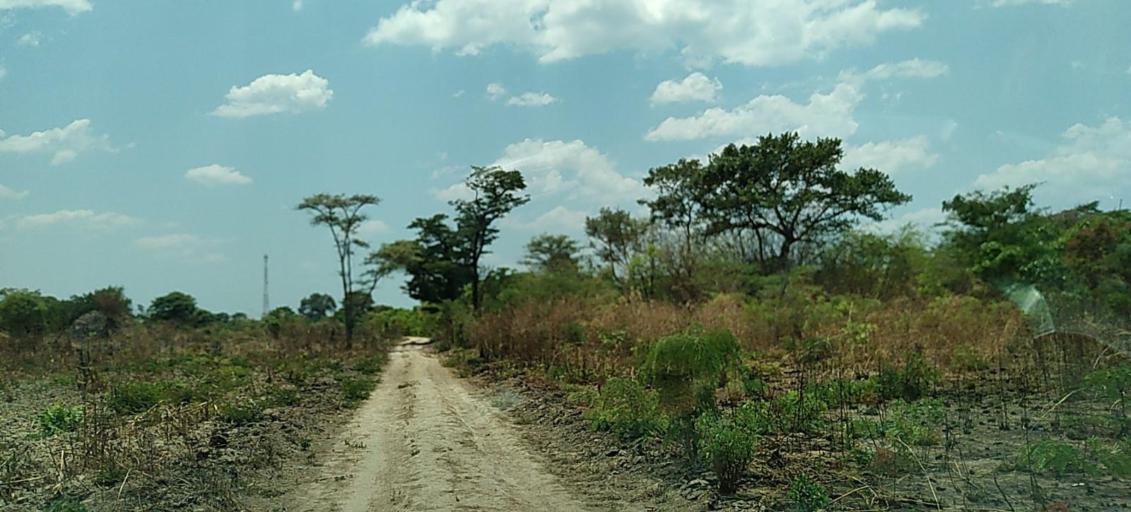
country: ZM
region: Copperbelt
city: Chililabombwe
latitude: -12.4529
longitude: 27.6758
